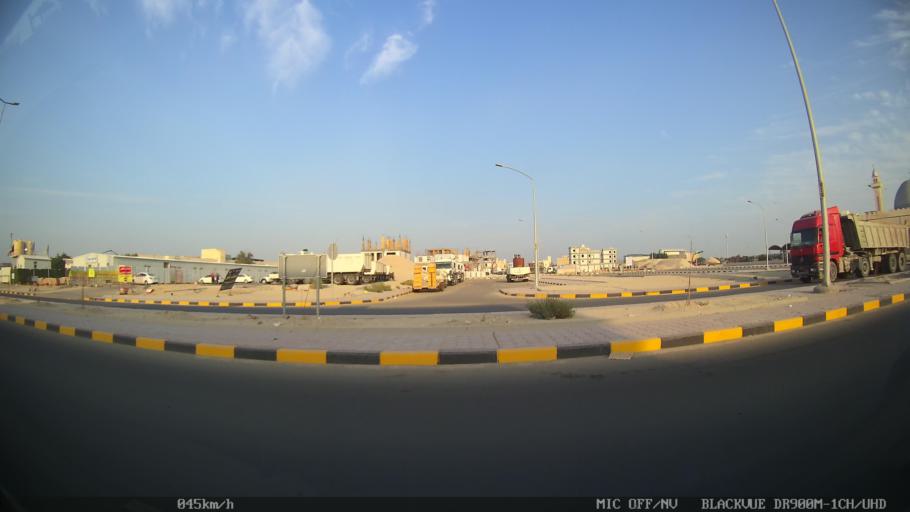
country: KW
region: Al Farwaniyah
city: Janub as Surrah
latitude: 29.2687
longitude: 47.9810
